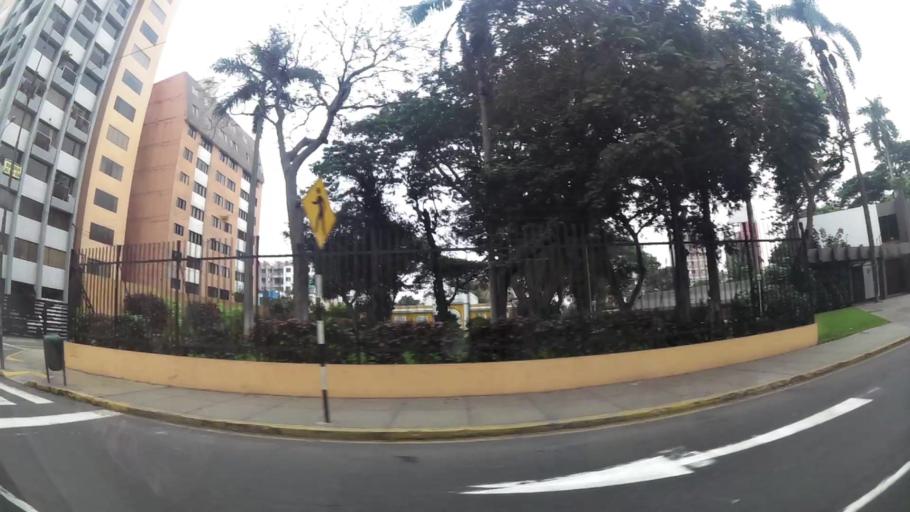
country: PE
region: Lima
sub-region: Lima
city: San Isidro
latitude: -12.1190
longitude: -77.0379
